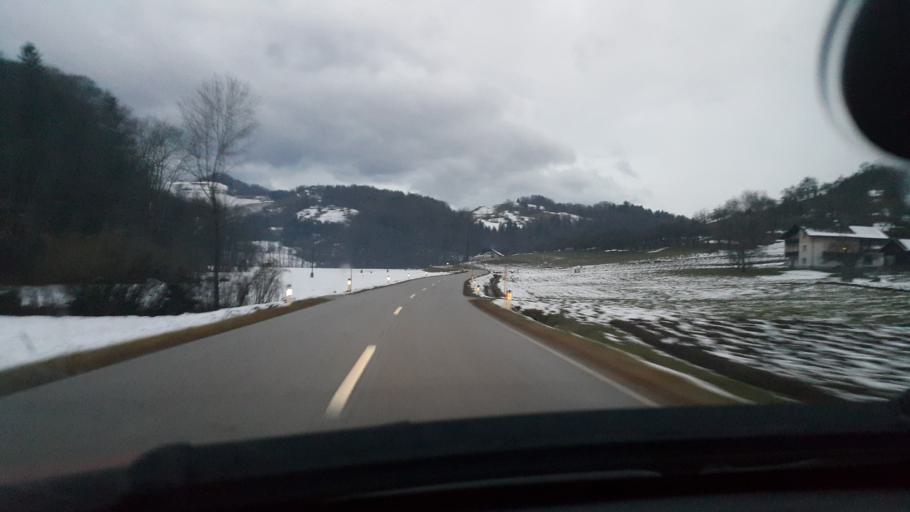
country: AT
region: Styria
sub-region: Politischer Bezirk Leibnitz
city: Sulztal an der Weinstrasse
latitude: 46.6469
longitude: 15.5616
